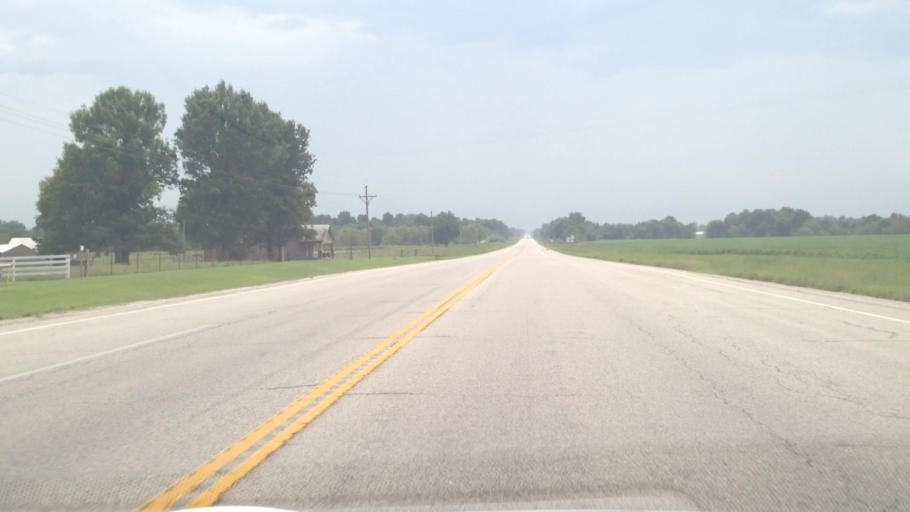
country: US
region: Kansas
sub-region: Cherokee County
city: Galena
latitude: 37.1478
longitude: -94.7042
